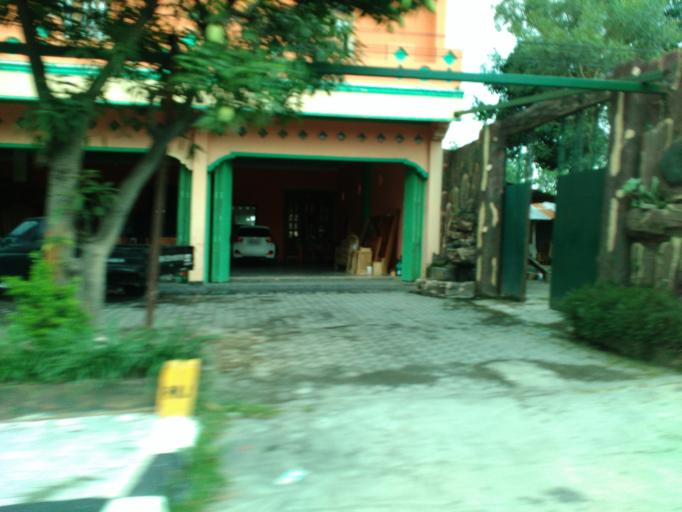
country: ID
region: Central Java
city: Gatak
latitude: -7.6086
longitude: 110.7017
